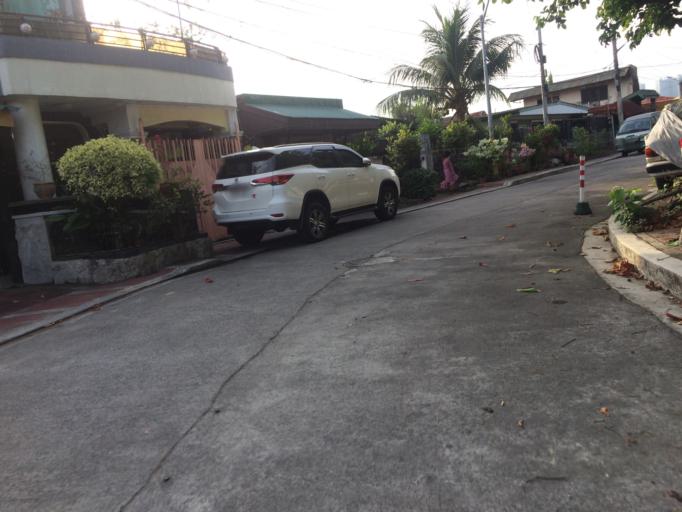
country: PH
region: Calabarzon
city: Bagong Pagasa
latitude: 14.6704
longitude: 121.0175
